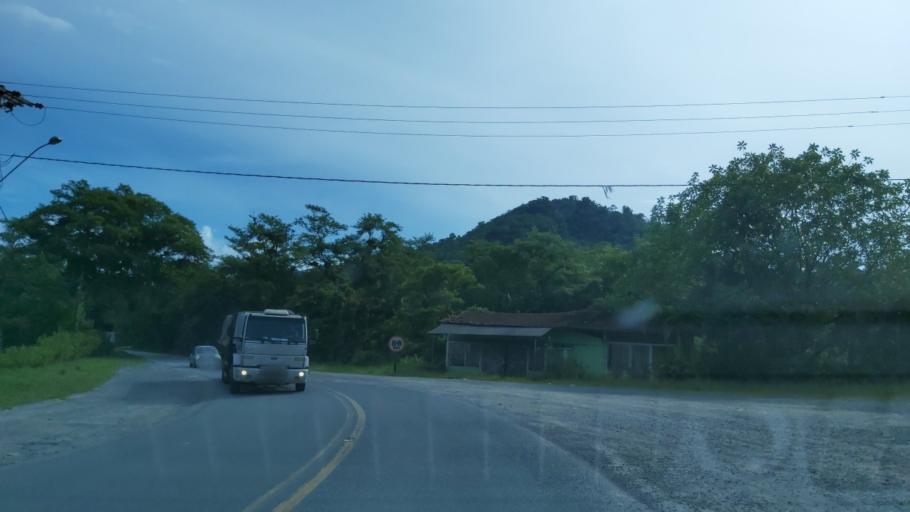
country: BR
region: Sao Paulo
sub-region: Miracatu
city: Miracatu
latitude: -24.0646
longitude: -47.5919
